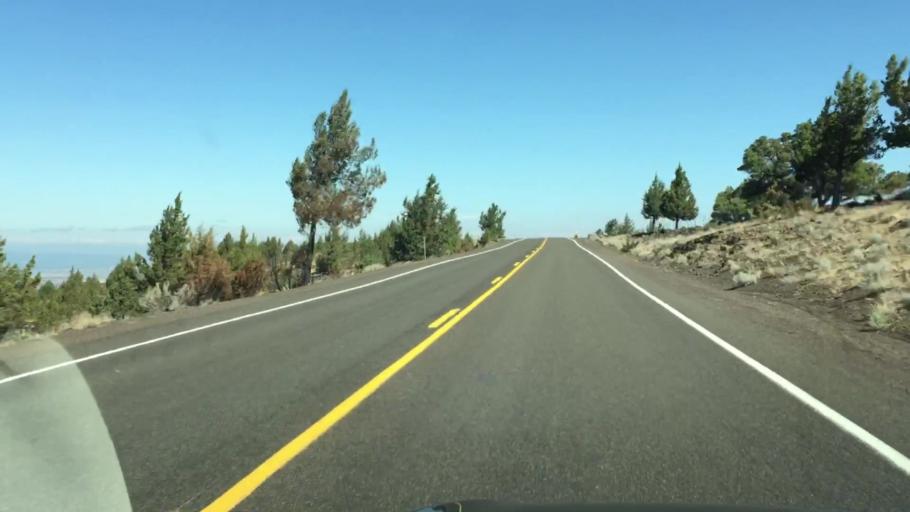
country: US
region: Oregon
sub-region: Jefferson County
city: Warm Springs
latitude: 45.0824
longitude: -121.0256
